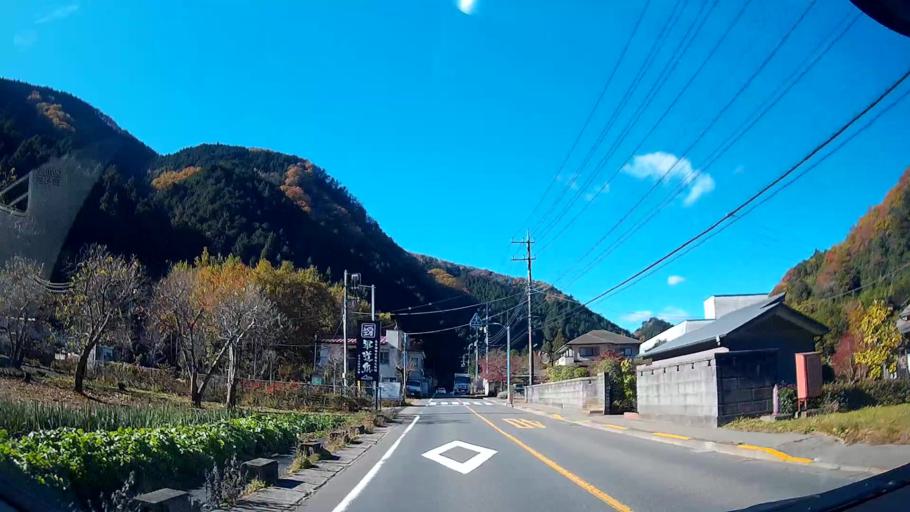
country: JP
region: Tokyo
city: Itsukaichi
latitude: 35.7238
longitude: 139.1785
